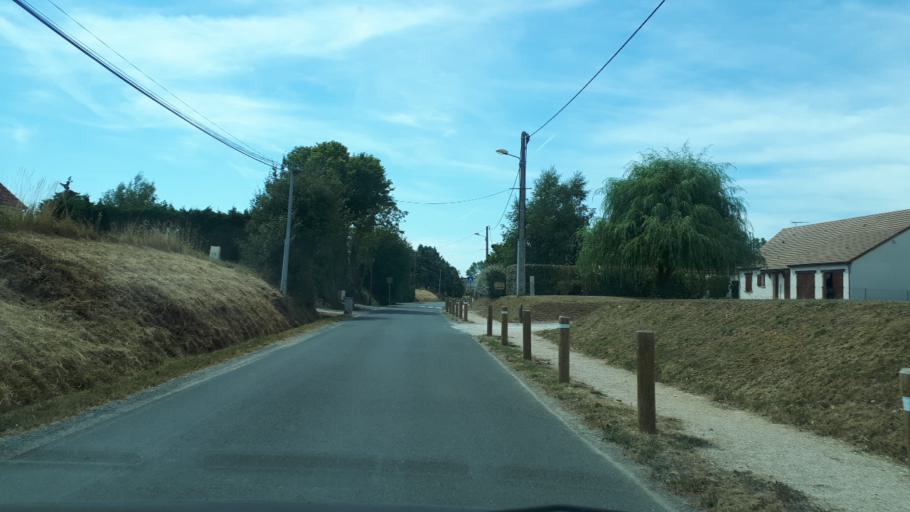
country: FR
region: Centre
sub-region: Departement du Loir-et-Cher
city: Contres
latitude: 47.3944
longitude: 1.3781
